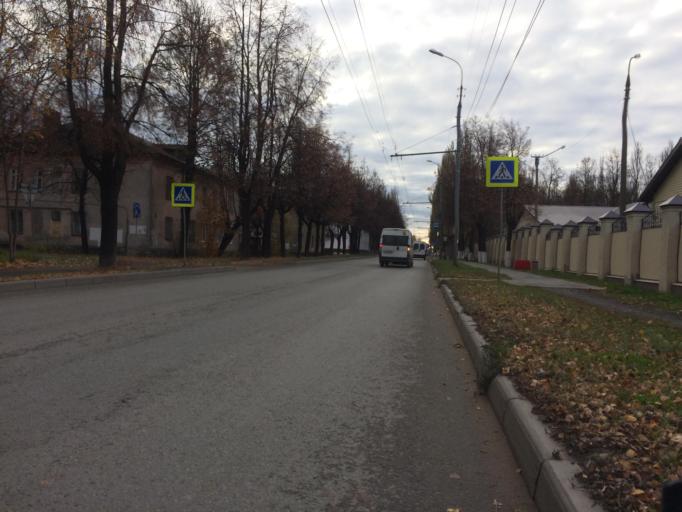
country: RU
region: Mariy-El
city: Yoshkar-Ola
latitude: 56.6386
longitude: 47.8616
